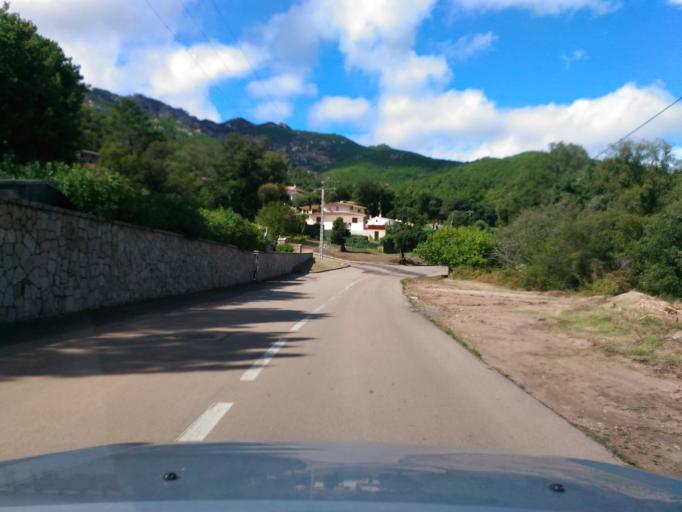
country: FR
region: Corsica
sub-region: Departement de la Corse-du-Sud
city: Porto-Vecchio
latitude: 41.7115
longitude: 9.3070
